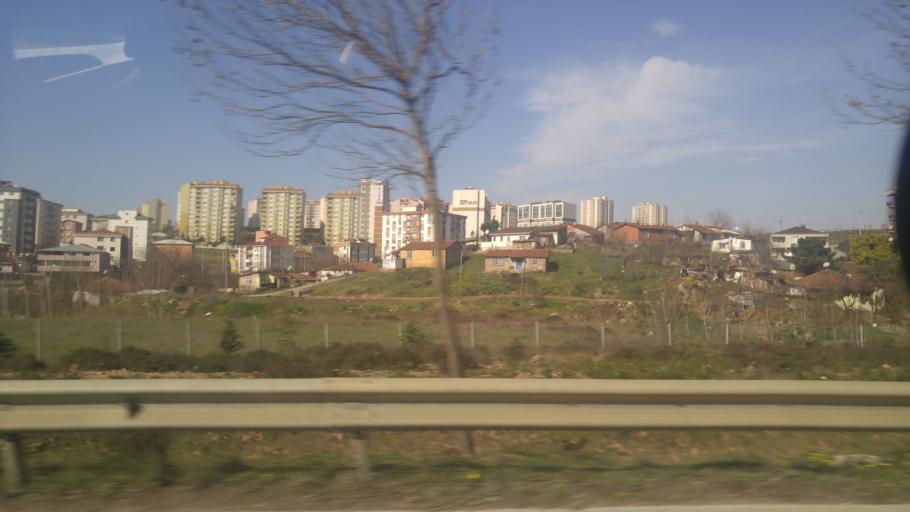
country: TR
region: Kocaeli
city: Darica
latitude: 40.8386
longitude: 29.3723
